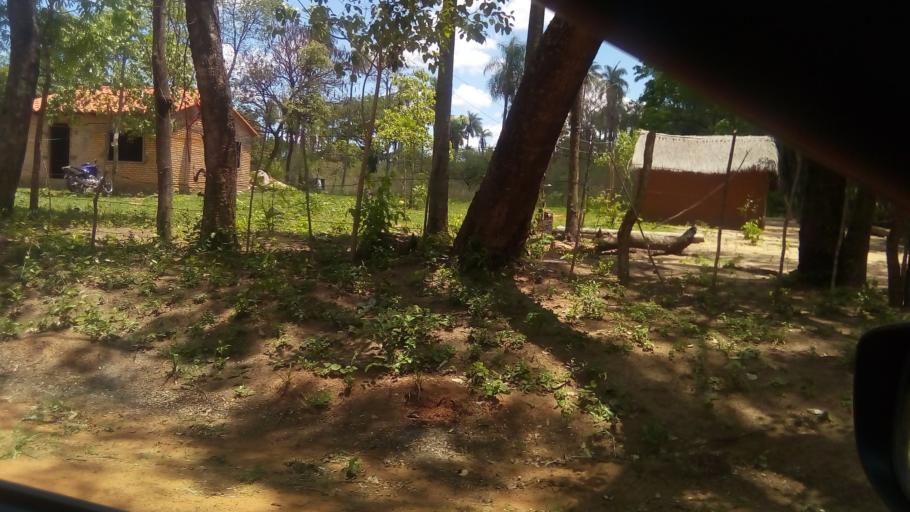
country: PY
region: Cordillera
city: Arroyos y Esteros
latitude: -24.9943
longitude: -57.2148
